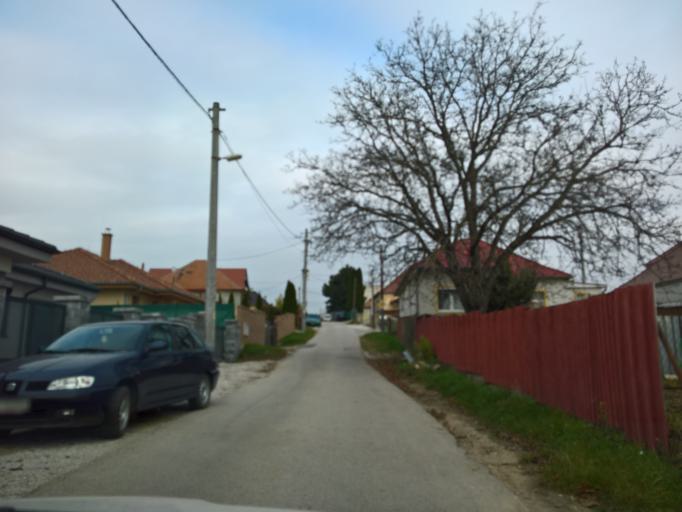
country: SK
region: Nitriansky
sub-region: Okres Nitra
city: Nitra
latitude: 48.2923
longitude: 18.1294
